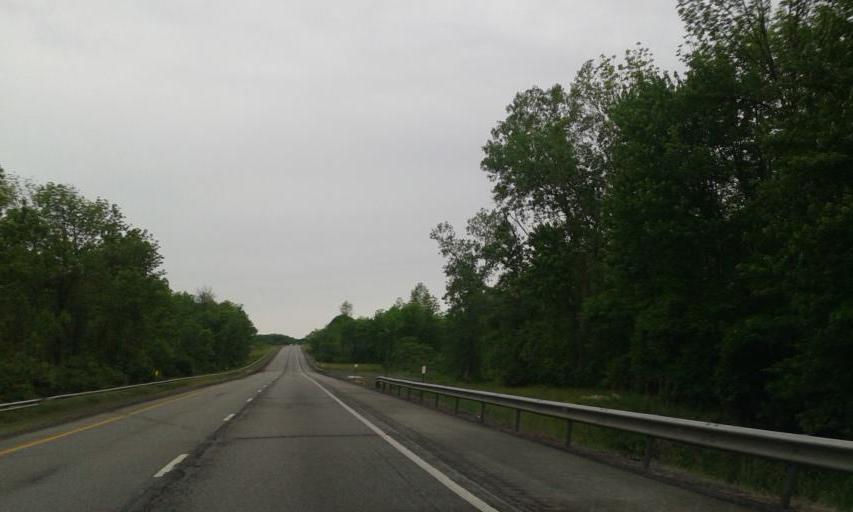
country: US
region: New York
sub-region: Genesee County
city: Bergen
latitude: 43.0298
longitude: -77.9247
